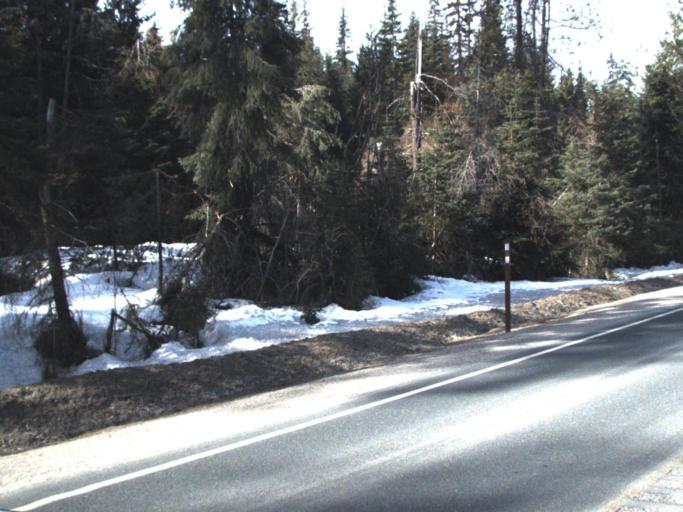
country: US
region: Washington
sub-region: Stevens County
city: Chewelah
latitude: 48.5400
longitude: -117.5984
